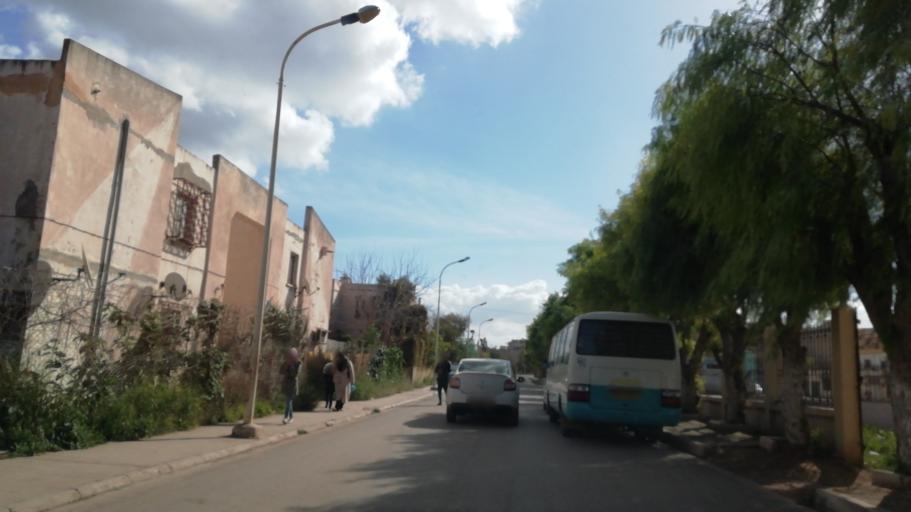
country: DZ
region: Oran
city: Es Senia
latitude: 35.6206
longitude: -0.5809
